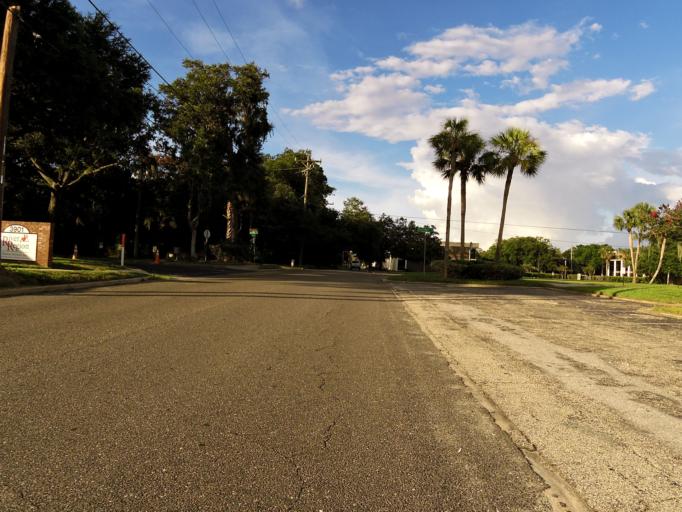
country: US
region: Florida
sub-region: Duval County
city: Jacksonville
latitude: 30.3015
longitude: -81.6217
